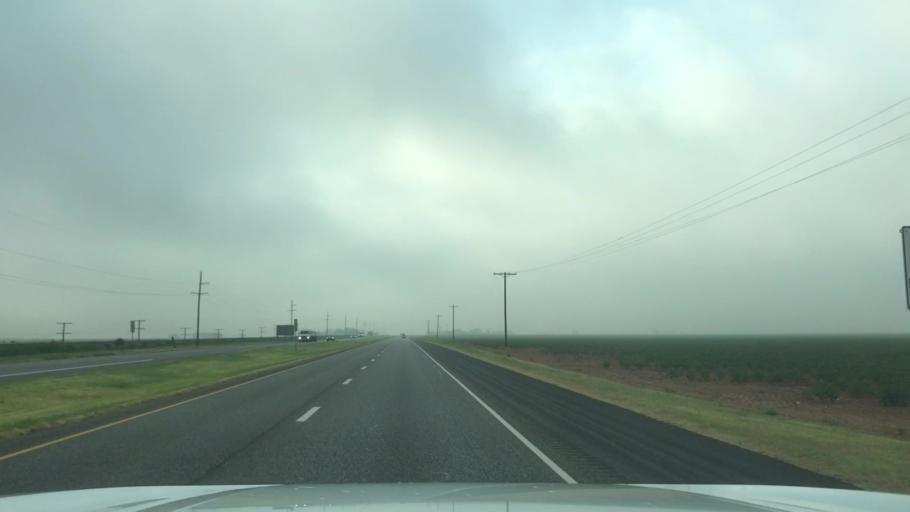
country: US
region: Texas
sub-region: Lubbock County
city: Ransom Canyon
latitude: 33.4900
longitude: -101.7240
